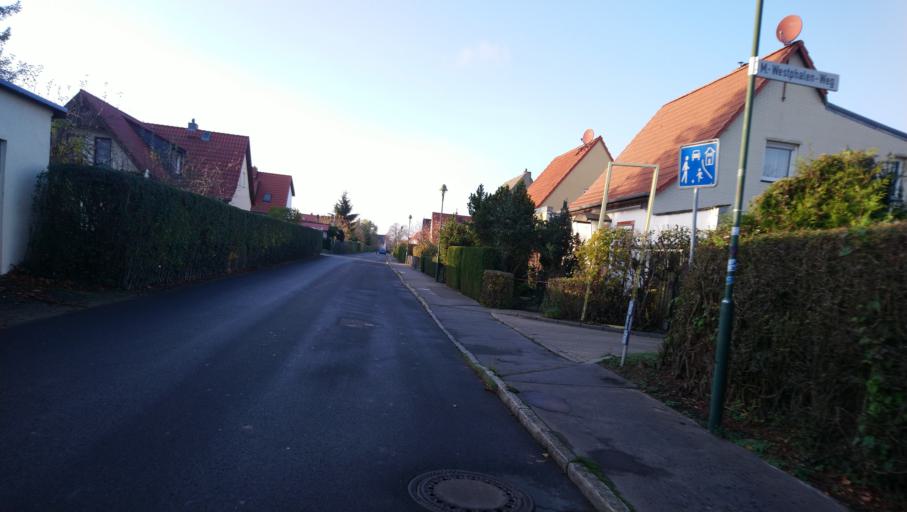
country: DE
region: Mecklenburg-Vorpommern
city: Kritzmow
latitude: 54.1027
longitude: 12.0823
